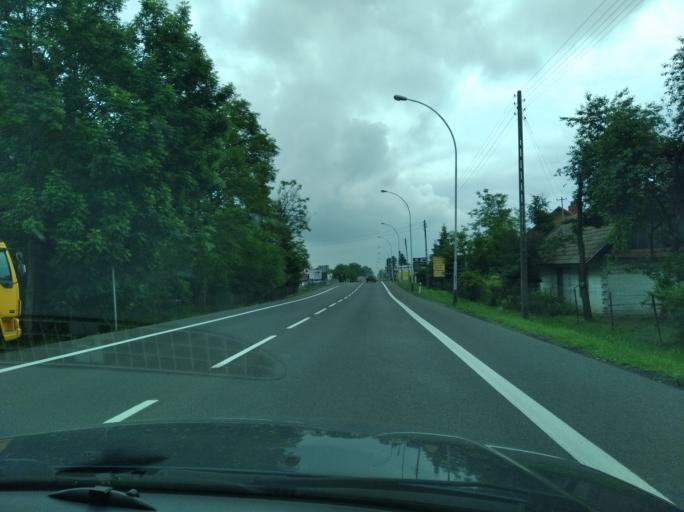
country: PL
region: Subcarpathian Voivodeship
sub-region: Powiat przeworski
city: Przeworsk
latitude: 50.0566
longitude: 22.5045
